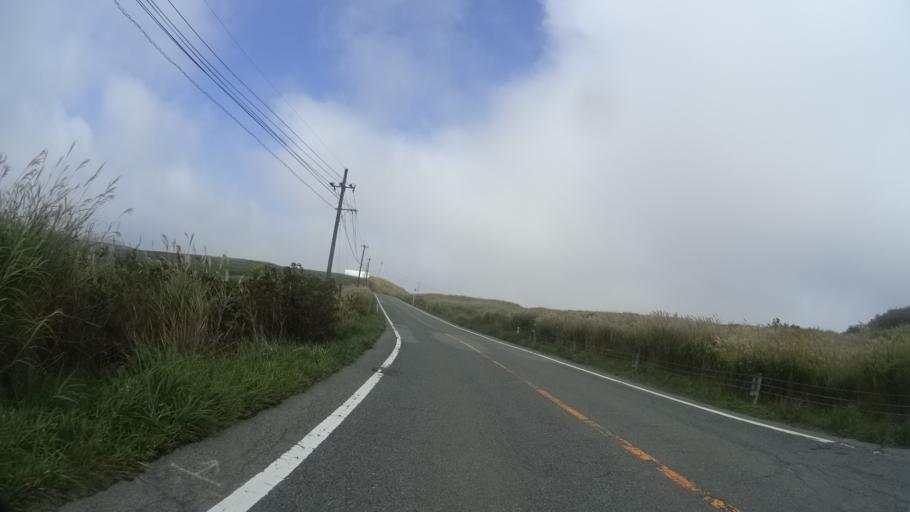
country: JP
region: Kumamoto
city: Aso
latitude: 32.9658
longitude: 131.0017
